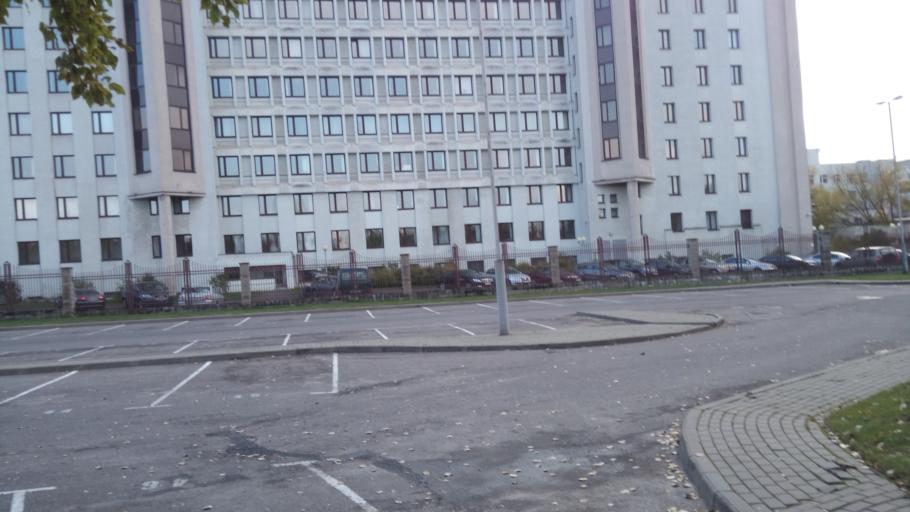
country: BY
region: Minsk
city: Minsk
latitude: 53.8869
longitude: 27.5593
